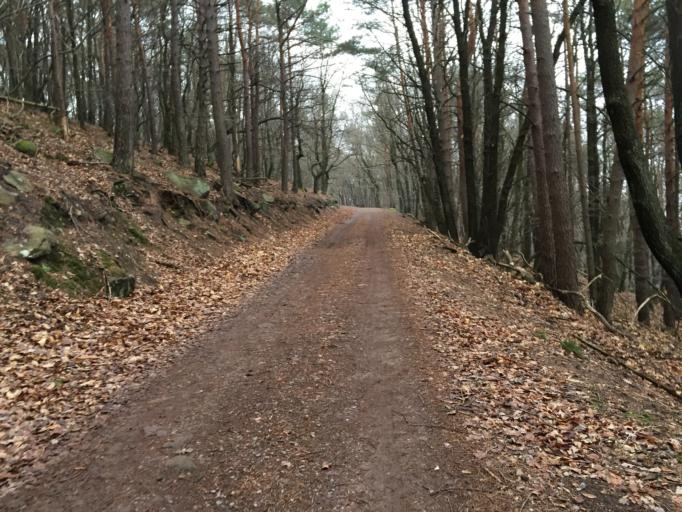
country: DE
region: Rheinland-Pfalz
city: Neustadt
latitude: 49.3365
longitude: 8.1108
